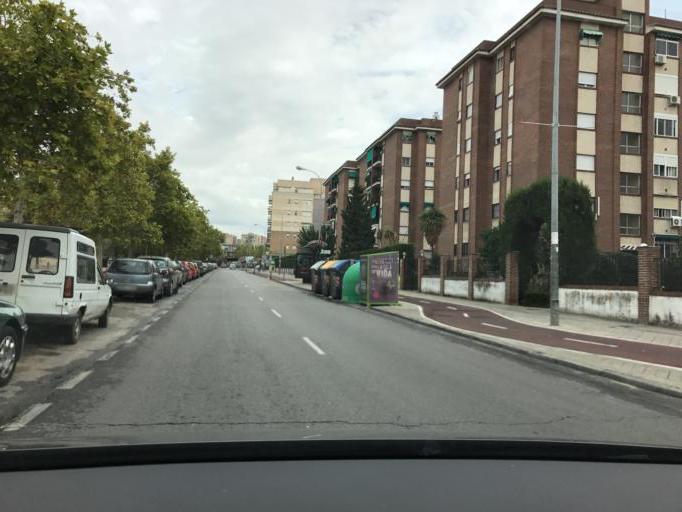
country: ES
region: Andalusia
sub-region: Provincia de Granada
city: Granada
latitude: 37.1969
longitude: -3.6097
